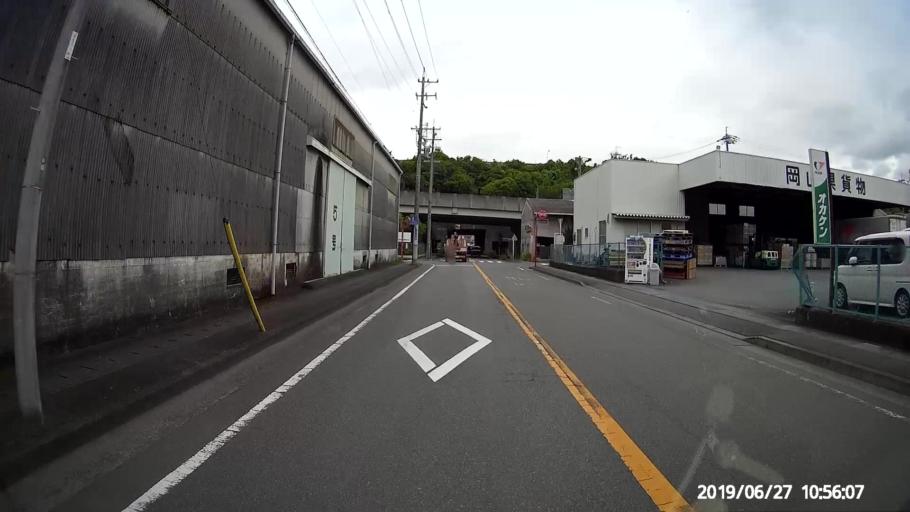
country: JP
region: Shizuoka
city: Shizuoka-shi
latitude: 34.9293
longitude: 138.3664
